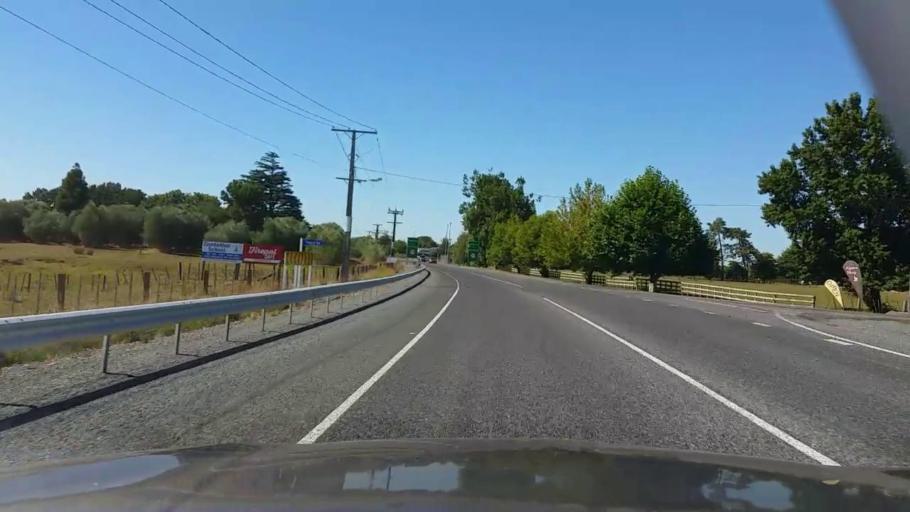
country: NZ
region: Waikato
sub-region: Hamilton City
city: Hamilton
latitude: -37.6678
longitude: 175.3010
